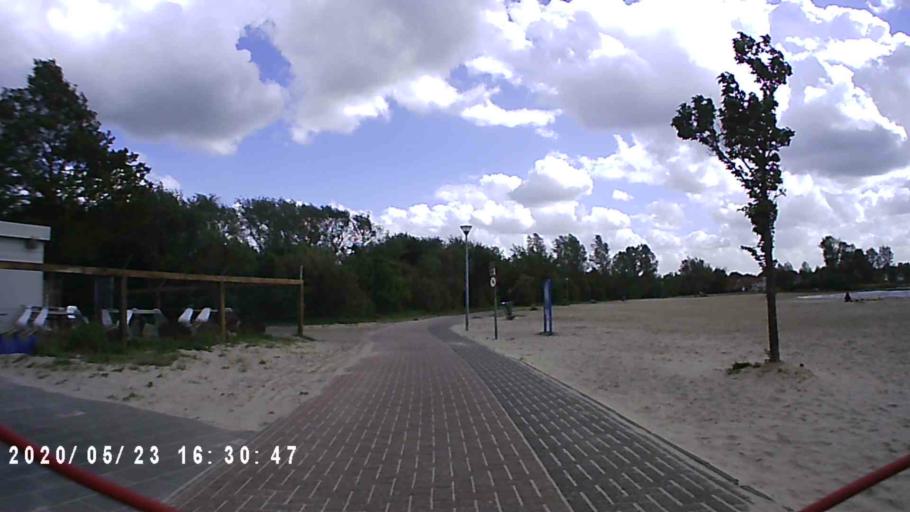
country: NL
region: Groningen
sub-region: Gemeente Appingedam
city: Appingedam
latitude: 53.2706
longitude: 6.8412
